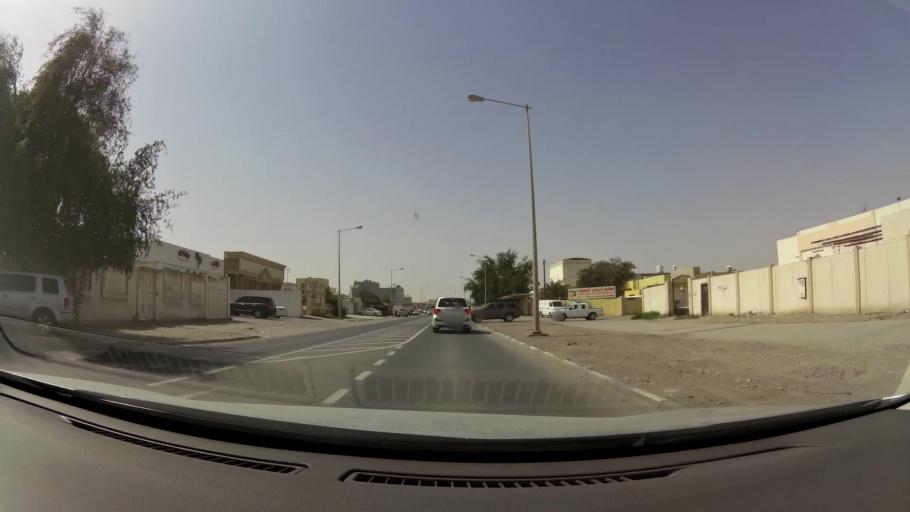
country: QA
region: Baladiyat Umm Salal
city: Umm Salal Muhammad
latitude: 25.3997
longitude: 51.4229
